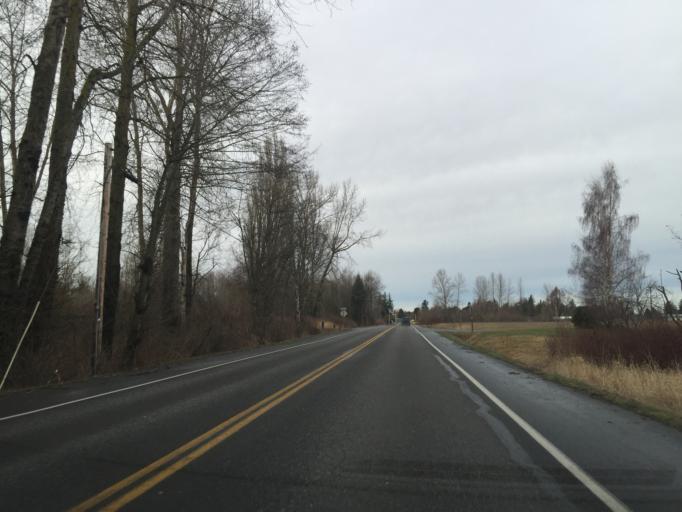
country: US
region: Washington
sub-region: Whatcom County
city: Marietta-Alderwood
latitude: 48.8265
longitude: -122.5356
